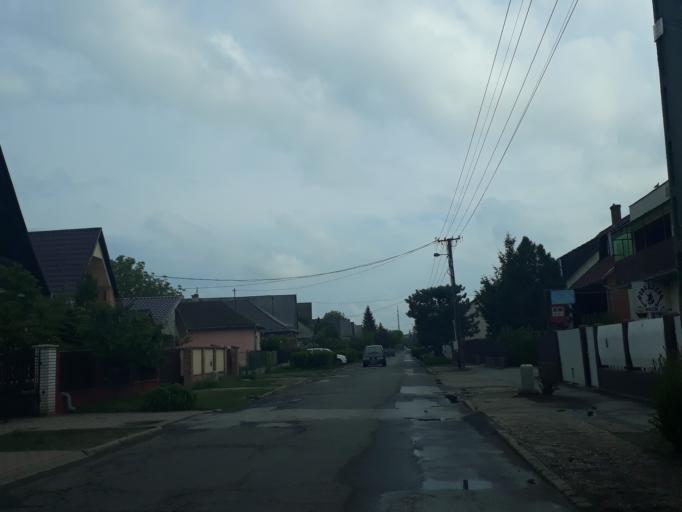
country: HU
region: Szabolcs-Szatmar-Bereg
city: Kisvarda
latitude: 48.2165
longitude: 22.0754
